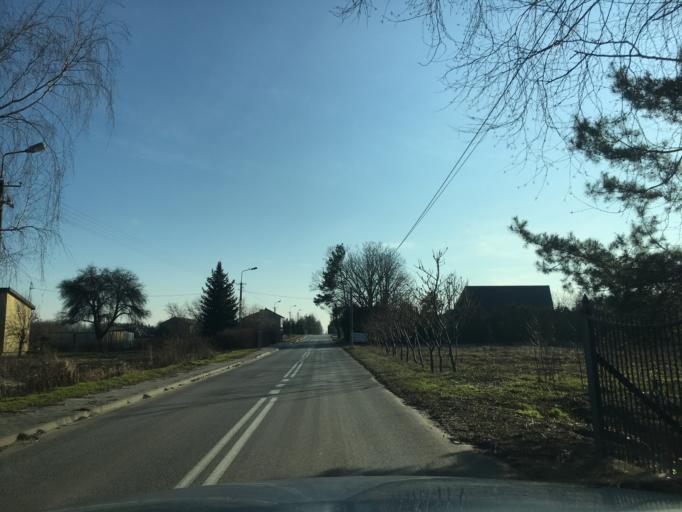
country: PL
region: Masovian Voivodeship
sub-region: Powiat pruszkowski
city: Nadarzyn
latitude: 52.0482
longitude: 20.8259
